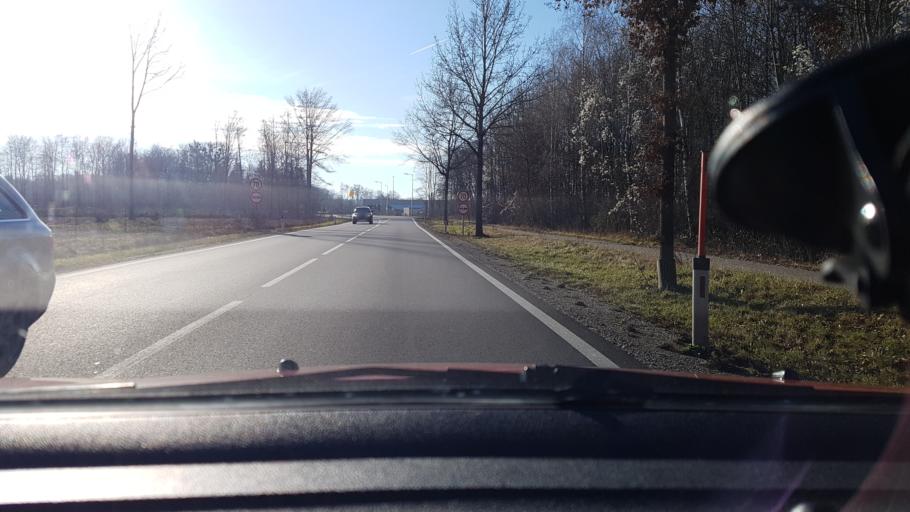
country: AT
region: Upper Austria
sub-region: Politischer Bezirk Braunau am Inn
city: Braunau am Inn
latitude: 48.2297
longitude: 13.0274
